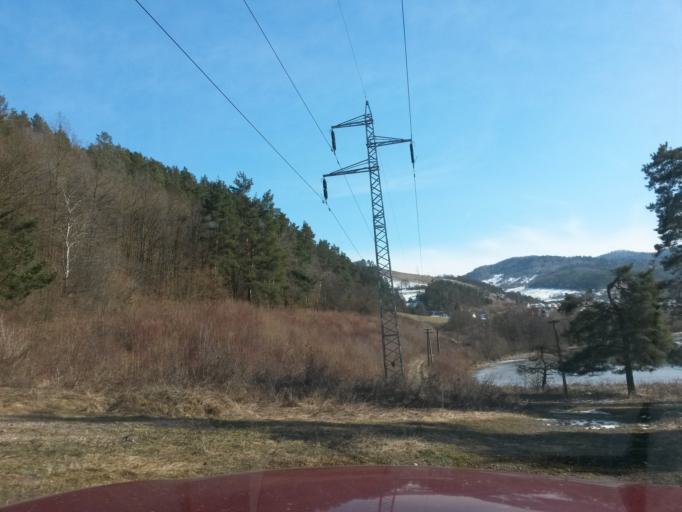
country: SK
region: Kosicky
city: Gelnica
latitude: 48.8667
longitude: 21.0092
